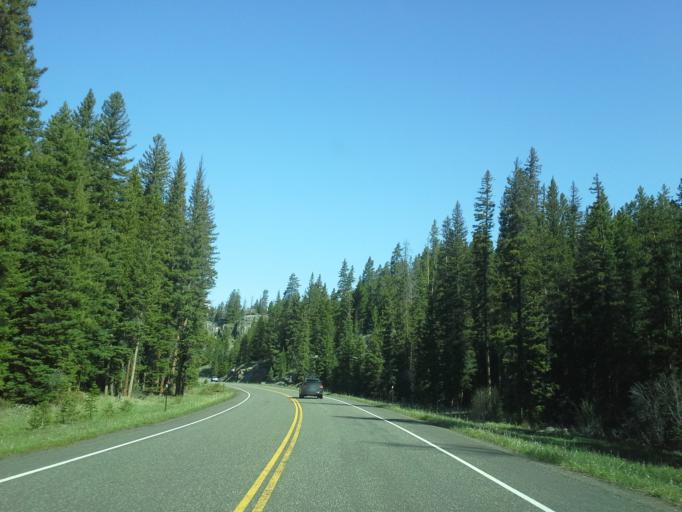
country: US
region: Montana
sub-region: Carbon County
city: Red Lodge
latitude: 44.9544
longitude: -109.7978
